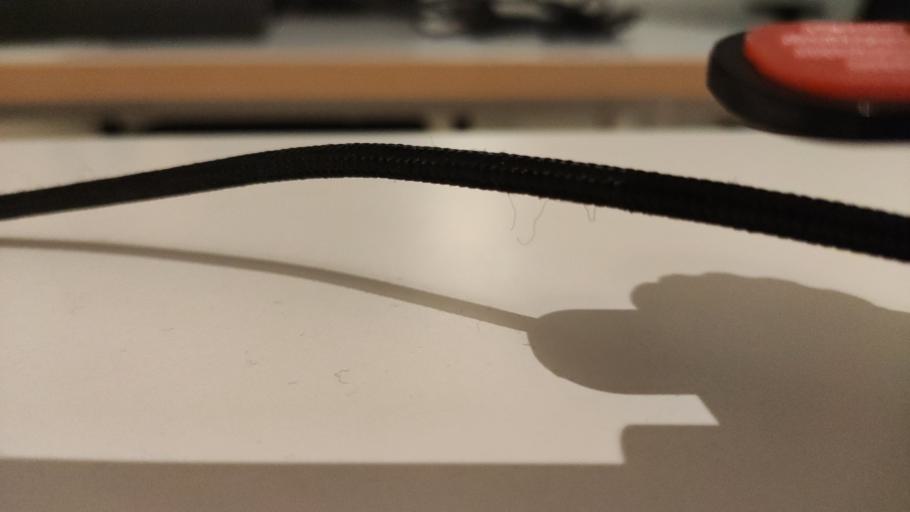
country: RU
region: Moskovskaya
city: Novoye
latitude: 55.6297
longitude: 38.9428
